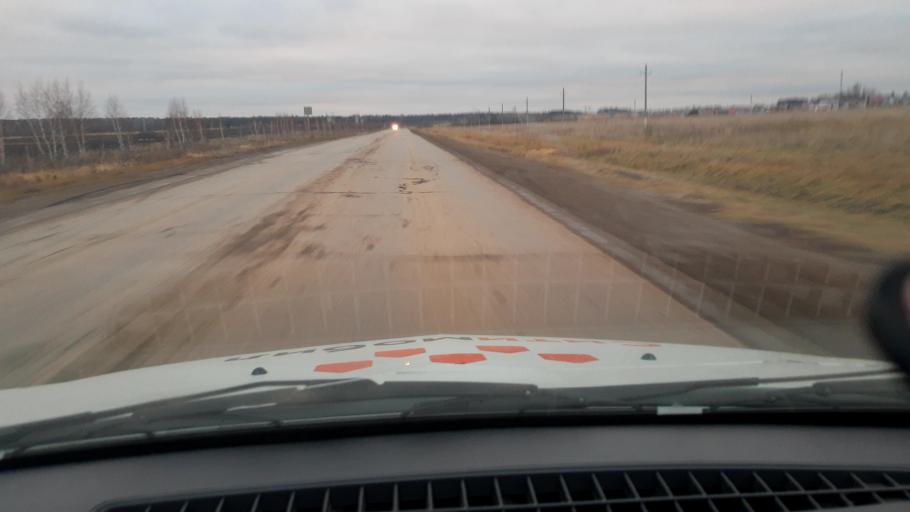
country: RU
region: Bashkortostan
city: Iglino
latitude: 54.7975
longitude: 56.4147
